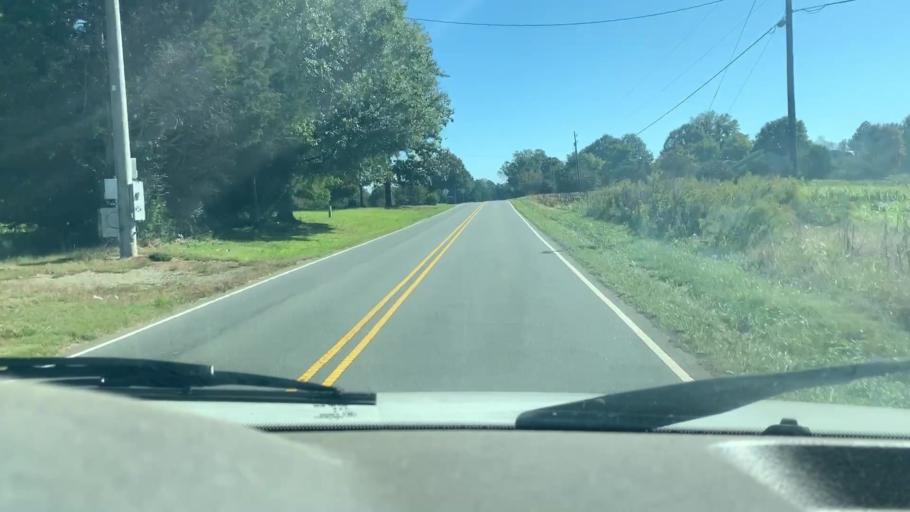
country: US
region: North Carolina
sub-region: Mecklenburg County
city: Cornelius
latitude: 35.4547
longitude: -80.8326
